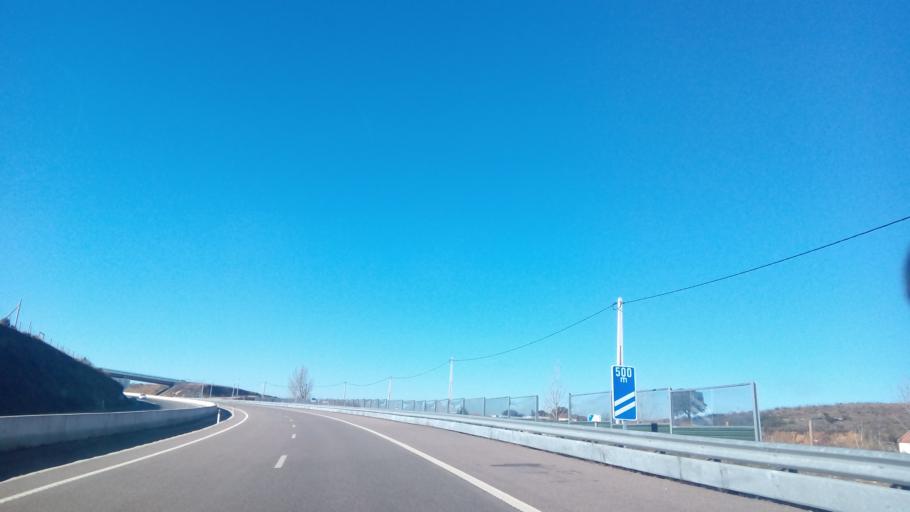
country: PT
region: Braganca
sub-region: Braganca Municipality
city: Braganca
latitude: 41.7897
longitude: -6.7107
